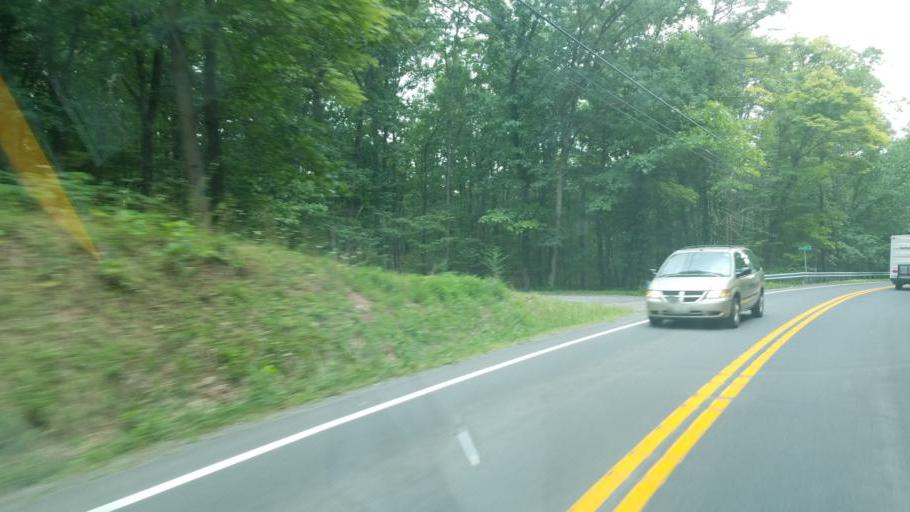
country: US
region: West Virginia
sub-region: Mineral County
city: Fort Ashby
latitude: 39.5296
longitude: -78.5181
